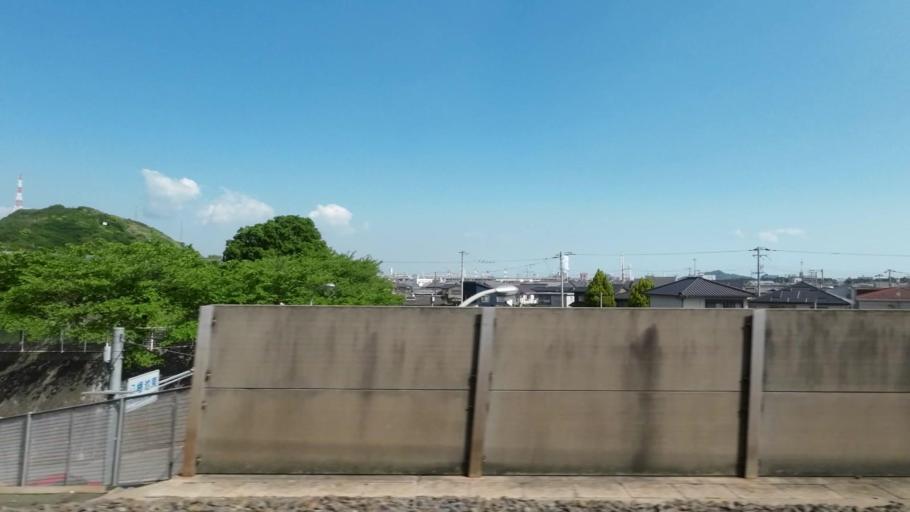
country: JP
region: Kagawa
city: Sakaidecho
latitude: 34.3118
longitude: 133.8437
